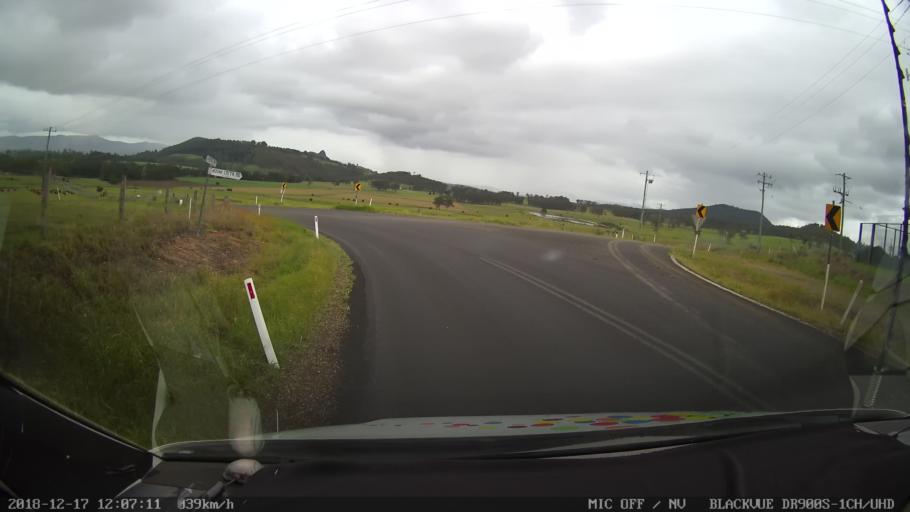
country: AU
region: New South Wales
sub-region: Kyogle
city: Kyogle
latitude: -28.4758
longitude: 152.5670
